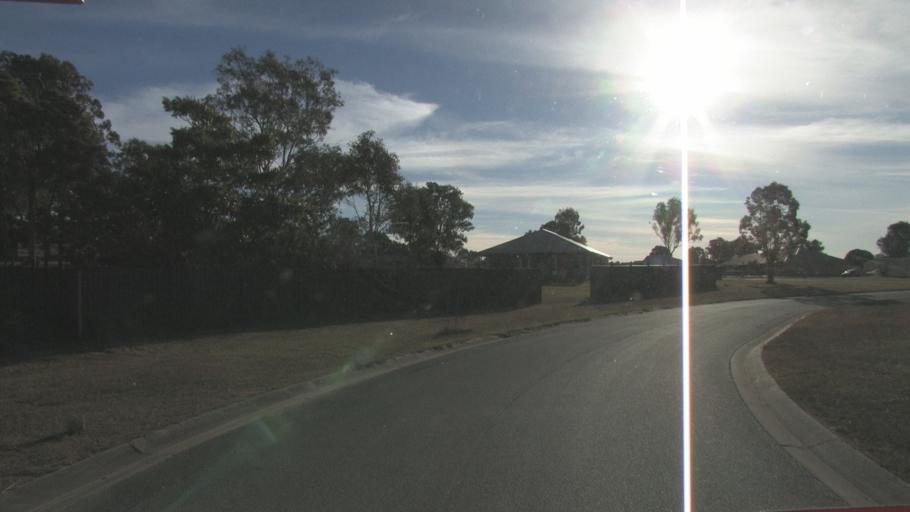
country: AU
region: Queensland
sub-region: Logan
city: North Maclean
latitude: -27.8290
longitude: 153.0078
